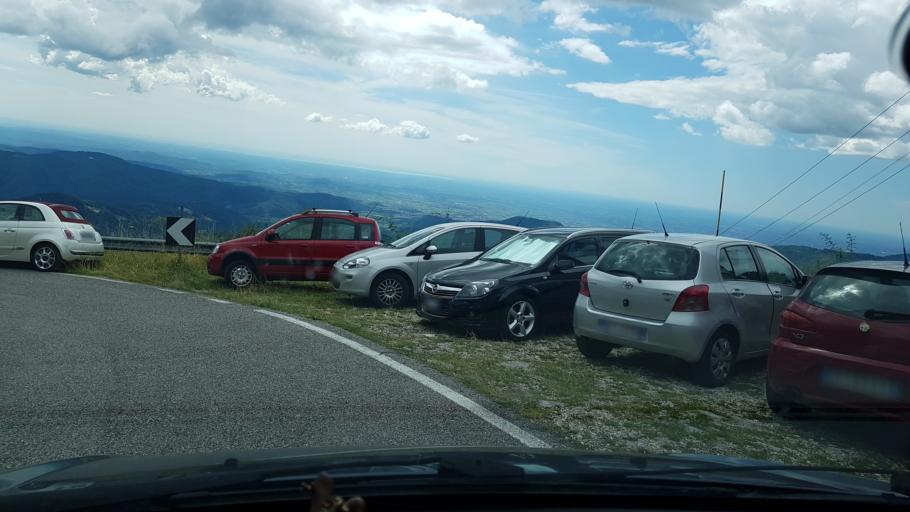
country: IT
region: Friuli Venezia Giulia
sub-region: Provincia di Udine
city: Savogna
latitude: 46.2026
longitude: 13.5369
